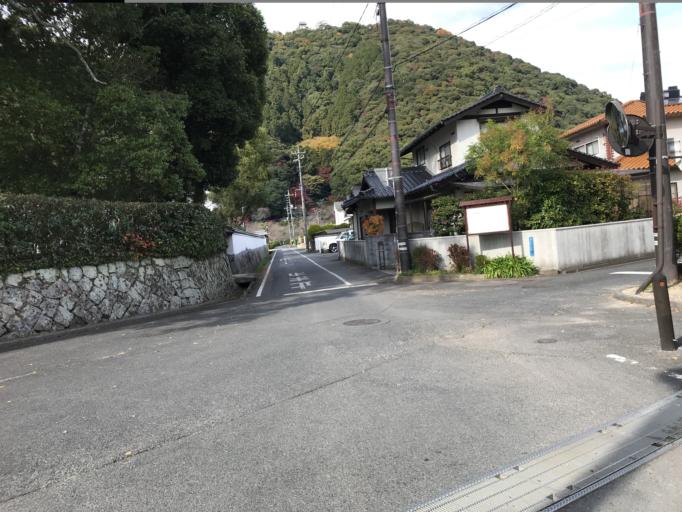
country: JP
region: Yamaguchi
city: Iwakuni
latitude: 34.1713
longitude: 132.1788
